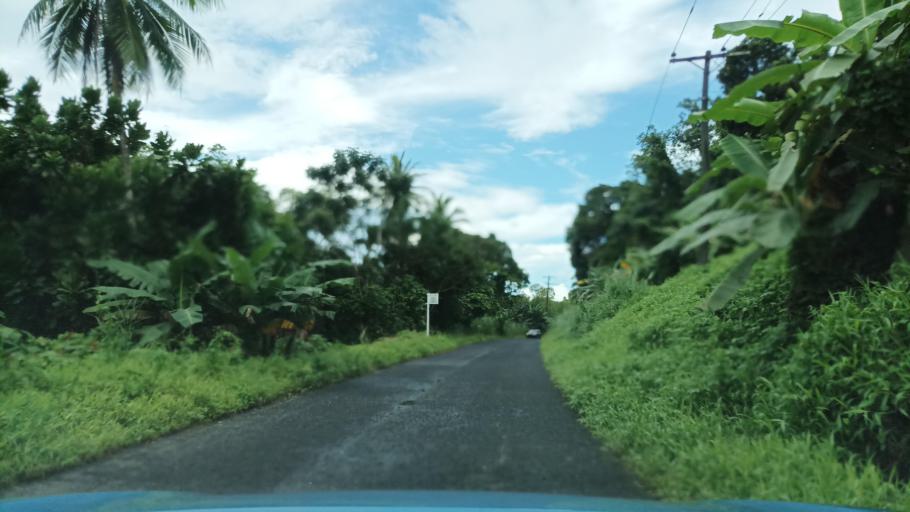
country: FM
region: Pohnpei
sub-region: Sokehs Municipality
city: Palikir - National Government Center
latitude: 6.8341
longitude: 158.1530
